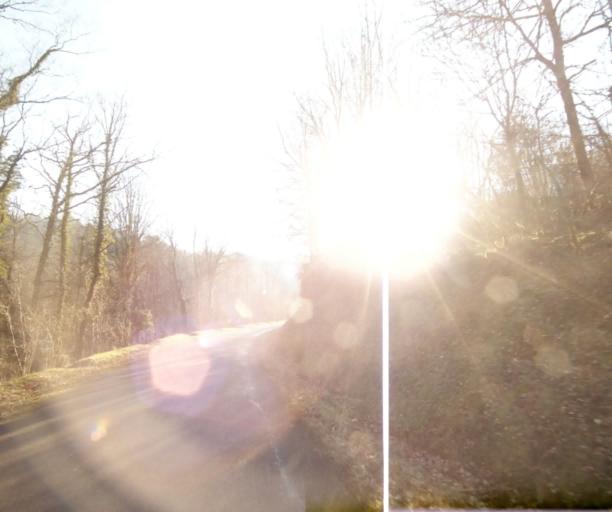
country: FR
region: Champagne-Ardenne
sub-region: Departement de la Haute-Marne
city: Chevillon
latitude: 48.5407
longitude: 5.1177
